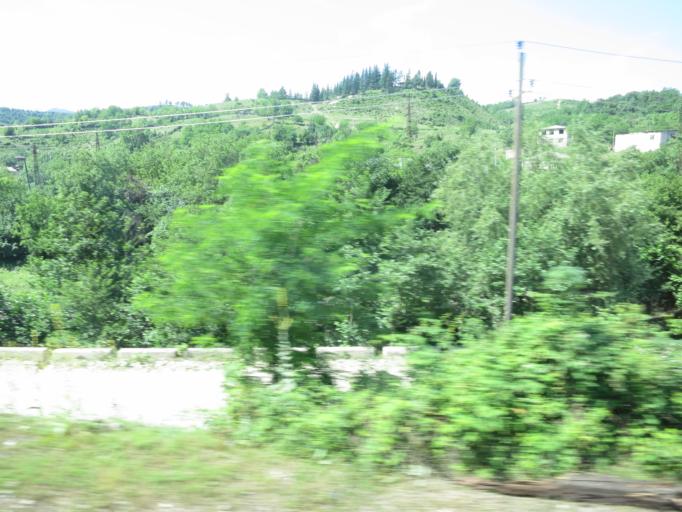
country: GE
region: Imereti
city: Kharagauli
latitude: 42.0278
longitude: 43.1972
